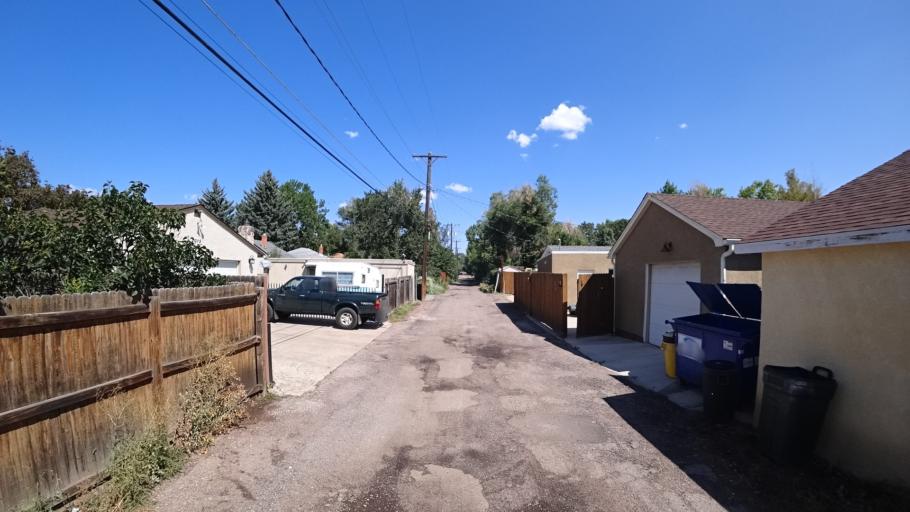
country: US
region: Colorado
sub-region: El Paso County
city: Colorado Springs
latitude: 38.8657
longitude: -104.8120
